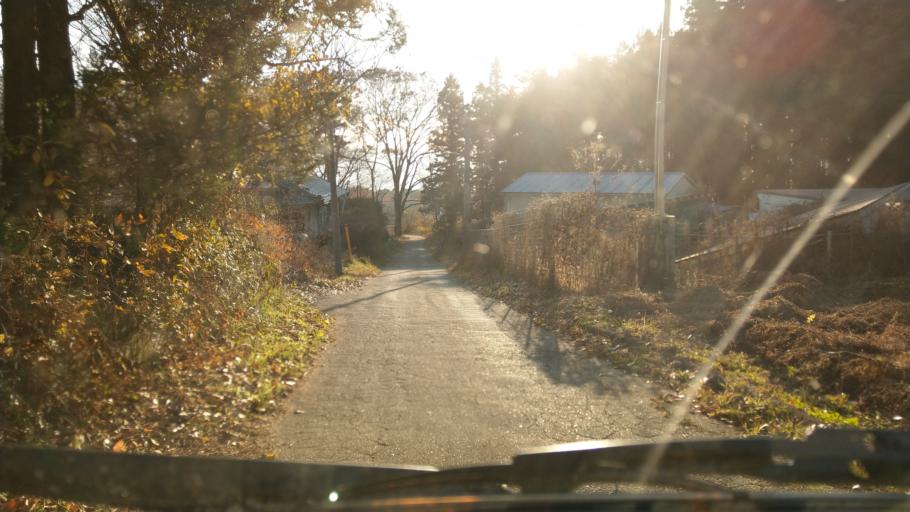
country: JP
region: Nagano
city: Komoro
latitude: 36.3531
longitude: 138.4552
